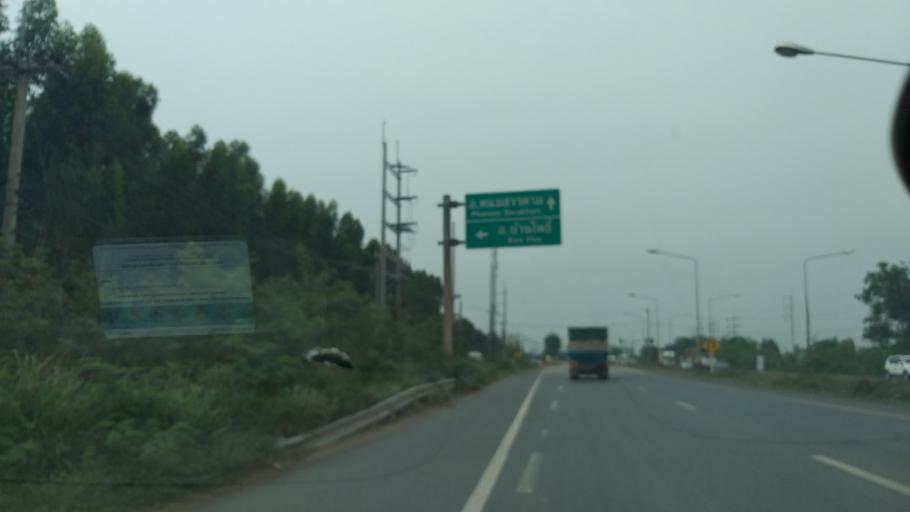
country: TH
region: Chachoengsao
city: Plaeng Yao
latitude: 13.5681
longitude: 101.2687
